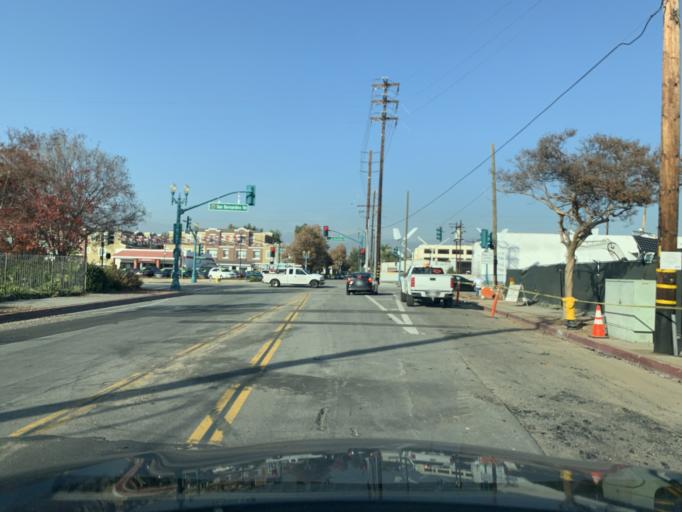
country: US
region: California
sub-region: Los Angeles County
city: Covina
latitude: 34.0896
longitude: -117.8924
